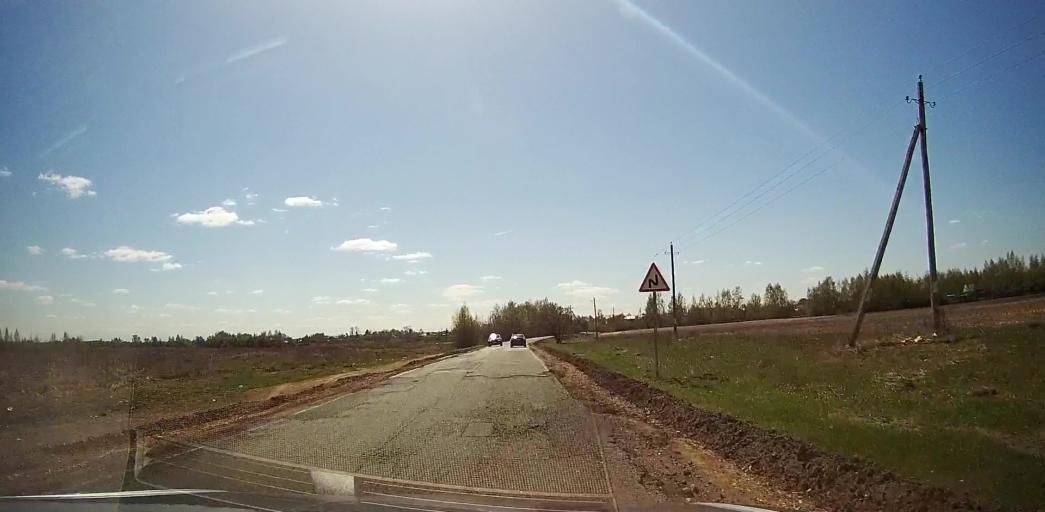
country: RU
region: Moskovskaya
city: Malyshevo
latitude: 55.4635
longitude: 38.3824
